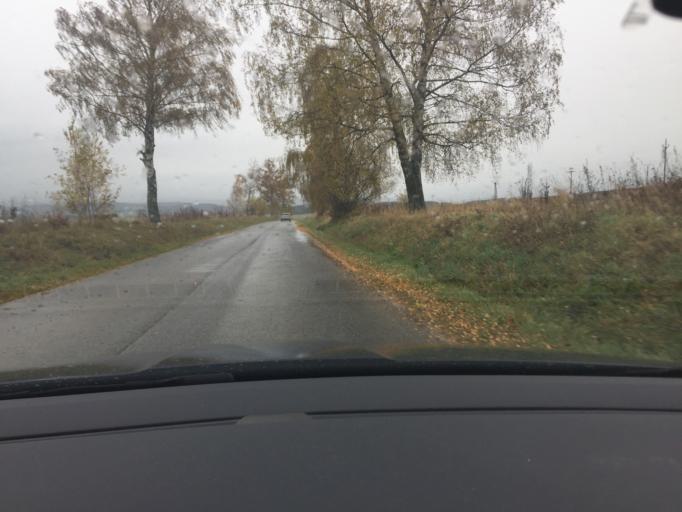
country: SK
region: Presovsky
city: Spisska Bela
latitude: 49.1943
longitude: 20.3841
